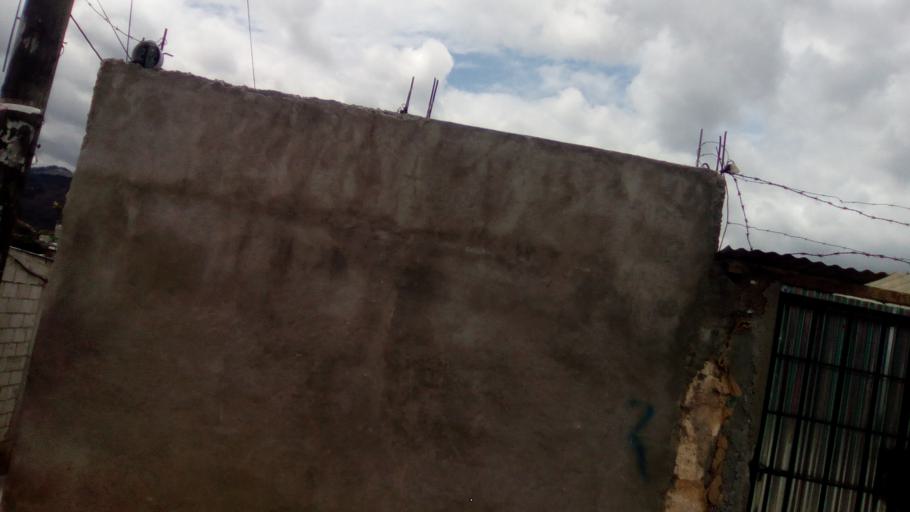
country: GT
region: Guatemala
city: Mixco
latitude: 14.5837
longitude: -90.6043
